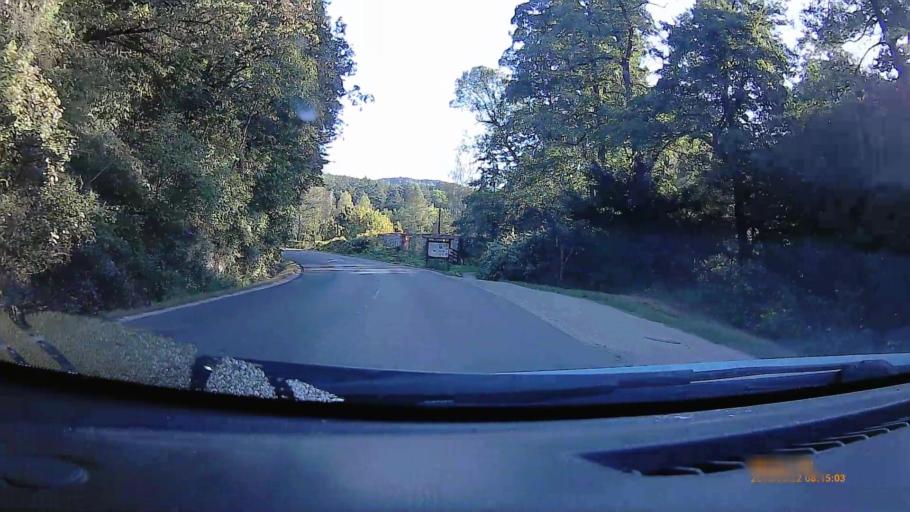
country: HU
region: Borsod-Abauj-Zemplen
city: Sajobabony
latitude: 48.1146
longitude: 20.6536
